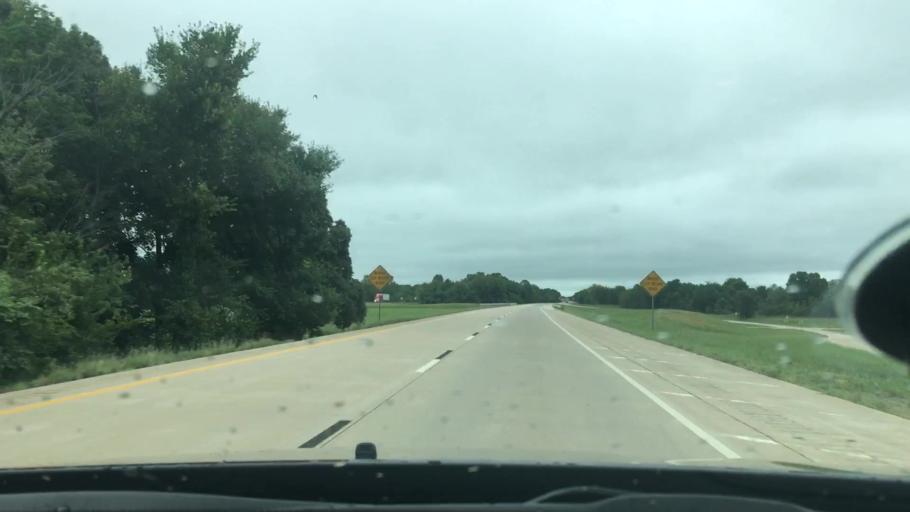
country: US
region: Oklahoma
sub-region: McIntosh County
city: Checotah
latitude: 35.4513
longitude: -95.7194
